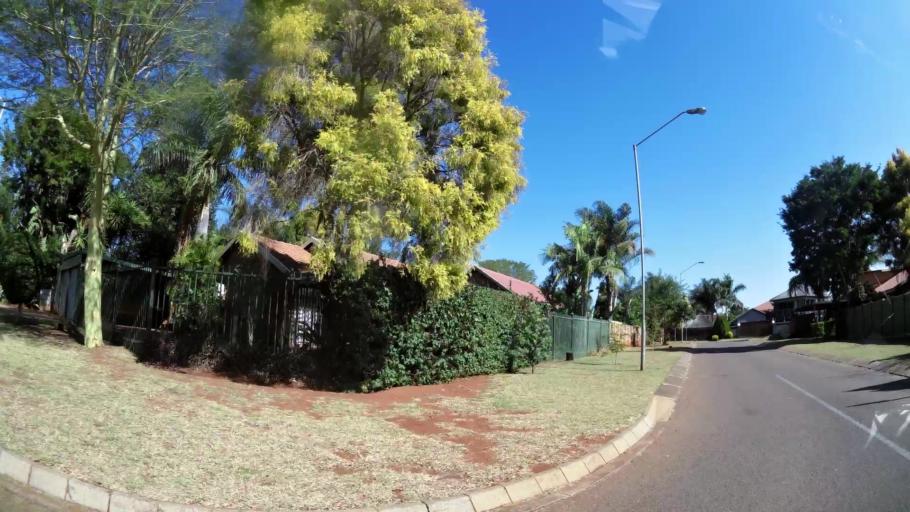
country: ZA
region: Gauteng
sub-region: City of Tshwane Metropolitan Municipality
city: Pretoria
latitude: -25.6535
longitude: 28.2560
